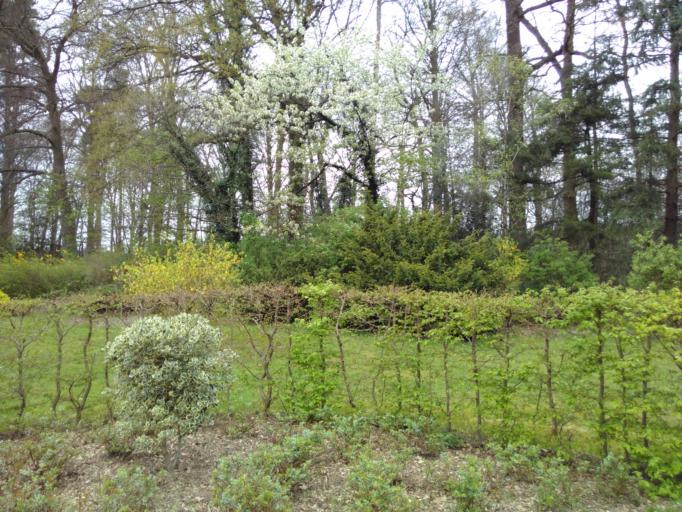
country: DE
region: North Rhine-Westphalia
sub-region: Regierungsbezirk Detmold
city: Hovelhof
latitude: 51.7803
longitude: 8.6129
